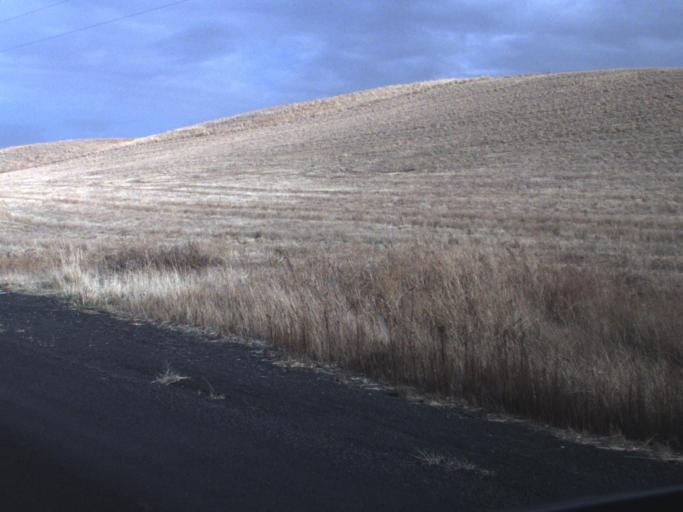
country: US
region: Washington
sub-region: Lincoln County
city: Davenport
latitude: 47.5236
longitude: -118.2087
